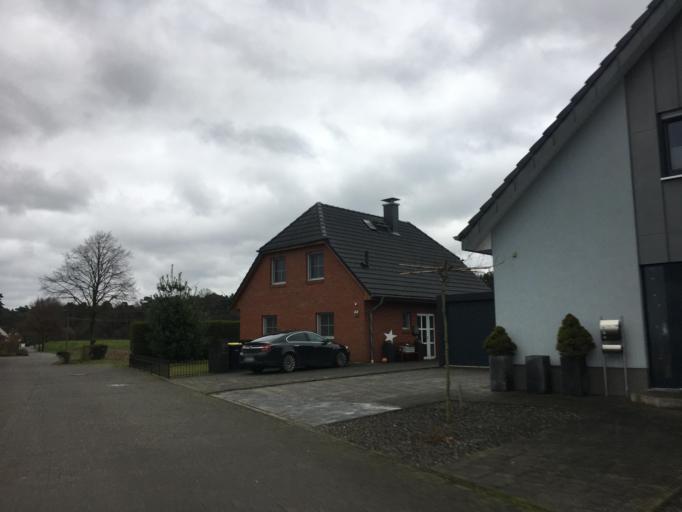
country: DE
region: North Rhine-Westphalia
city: Olfen
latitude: 51.7328
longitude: 7.2941
